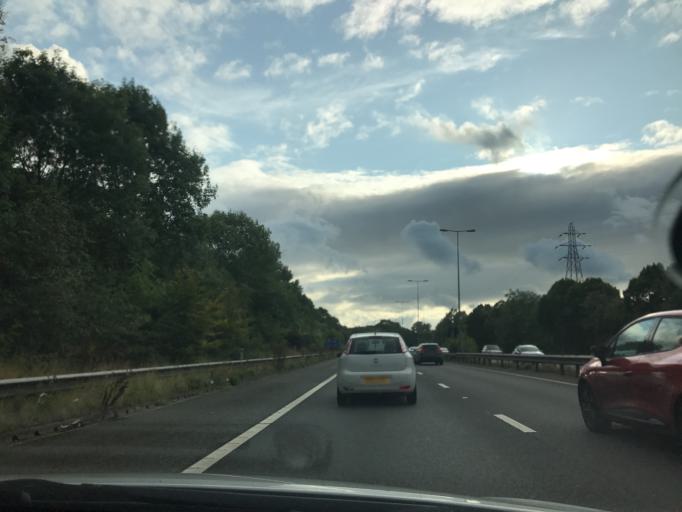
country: GB
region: England
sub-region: Cheshire West and Chester
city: Ellesmere Port
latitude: 53.2970
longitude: -2.9232
